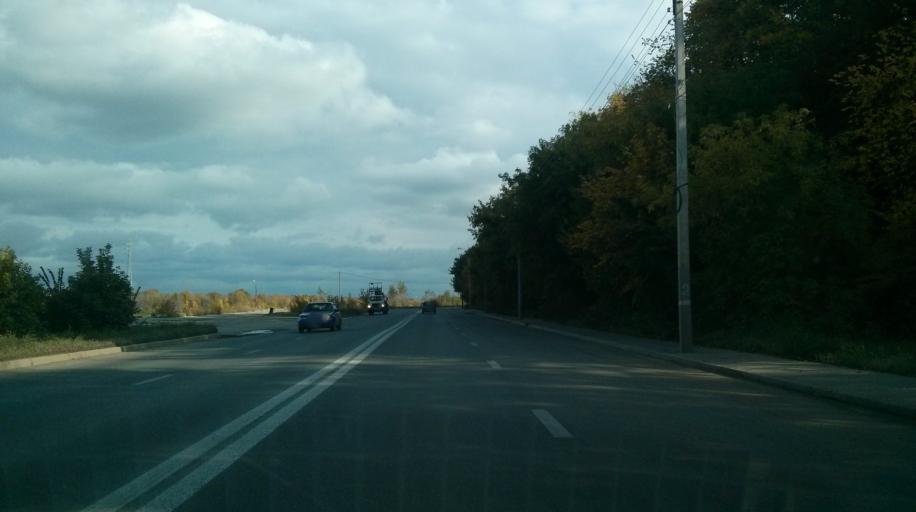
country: RU
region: Nizjnij Novgorod
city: Bor
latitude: 56.3204
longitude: 44.0704
